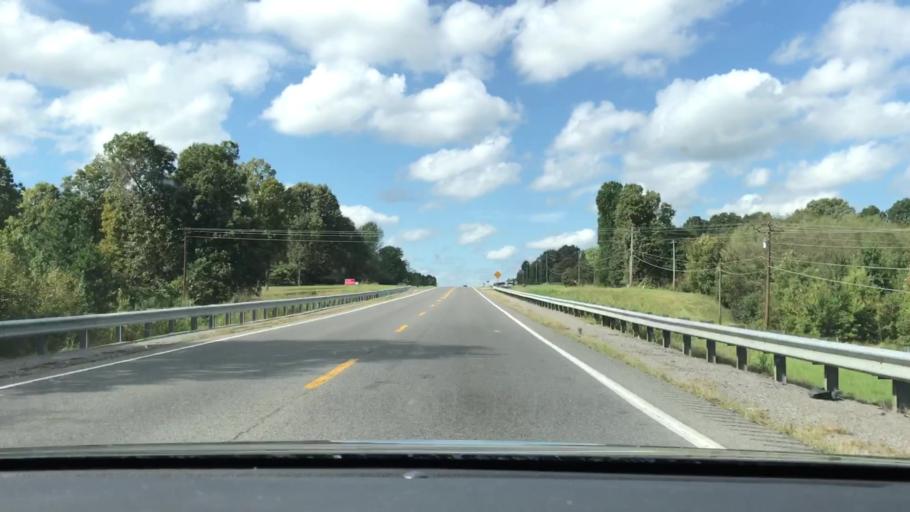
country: US
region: Kentucky
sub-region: Livingston County
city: Ledbetter
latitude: 37.0071
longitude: -88.4716
